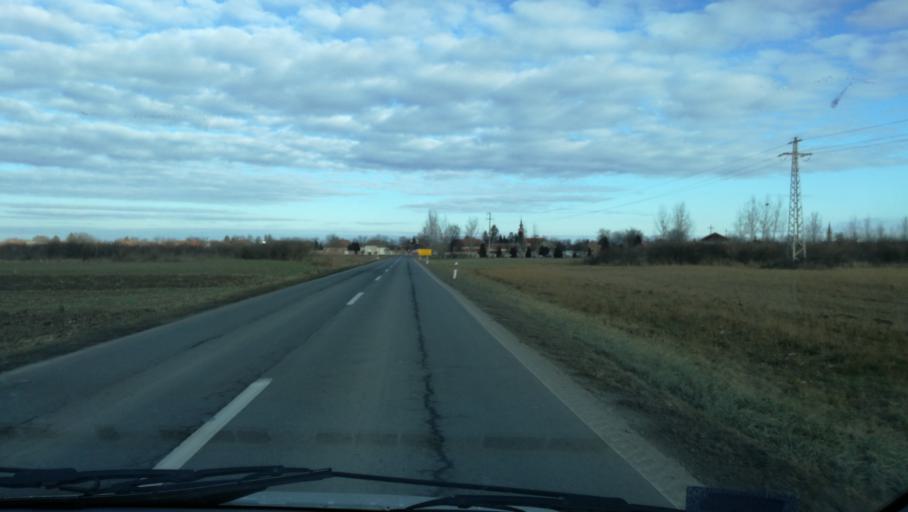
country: RS
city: Ostojicevo
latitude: 45.8824
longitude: 20.1653
